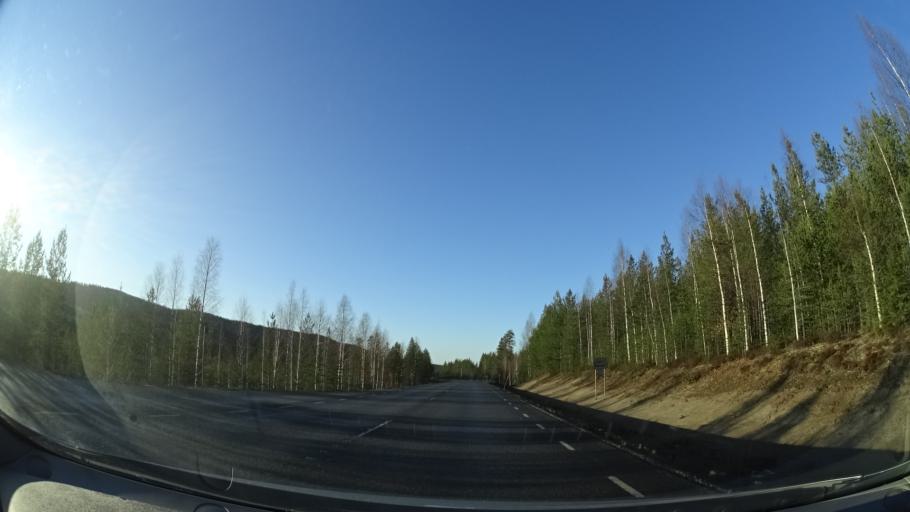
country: SE
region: Vaesterbotten
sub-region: Skelleftea Kommun
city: Langsele
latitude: 64.9190
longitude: 20.0866
